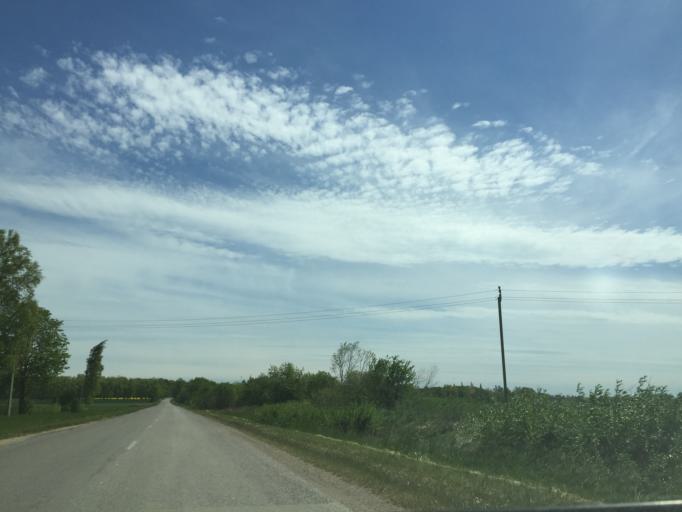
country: LT
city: Linkuva
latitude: 56.0358
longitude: 24.1548
